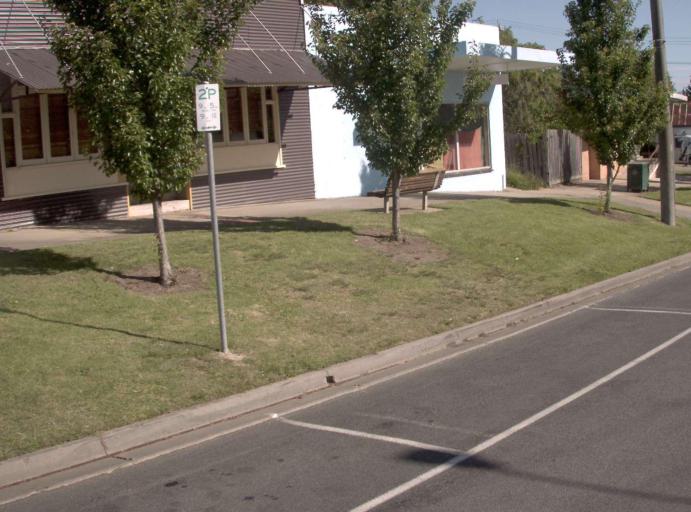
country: AU
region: Victoria
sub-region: East Gippsland
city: Lakes Entrance
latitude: -37.7082
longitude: 148.4544
